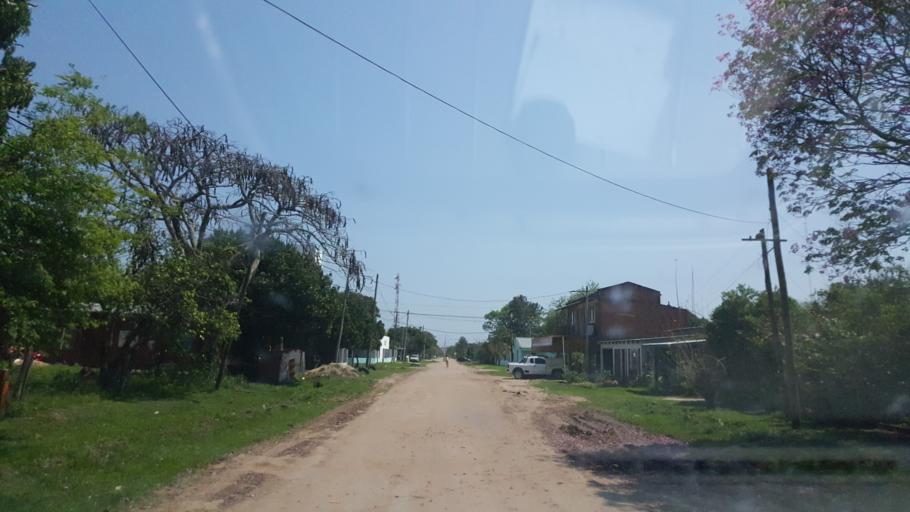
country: AR
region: Corrientes
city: Ita Ibate
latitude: -27.4265
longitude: -57.3303
